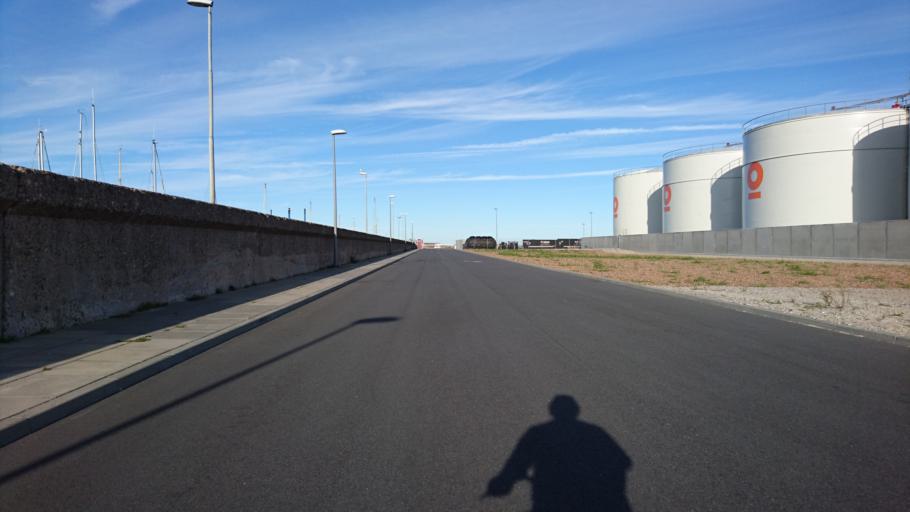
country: DK
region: North Denmark
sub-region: Frederikshavn Kommune
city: Skagen
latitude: 57.7148
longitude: 10.5871
